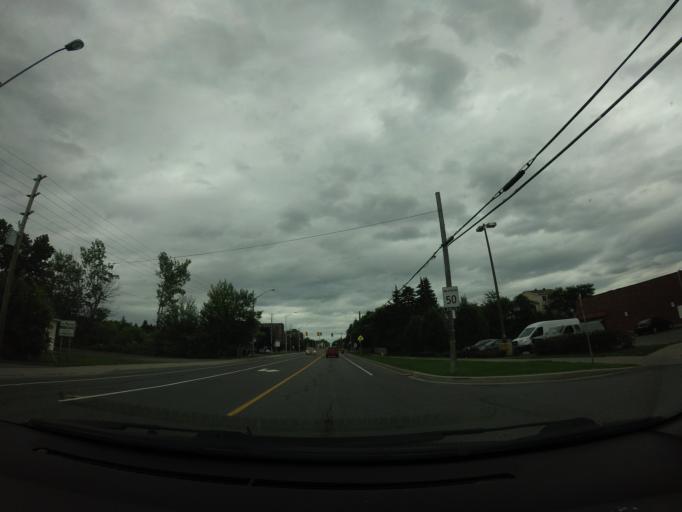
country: CA
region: Ontario
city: Ottawa
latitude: 45.4322
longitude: -75.5632
